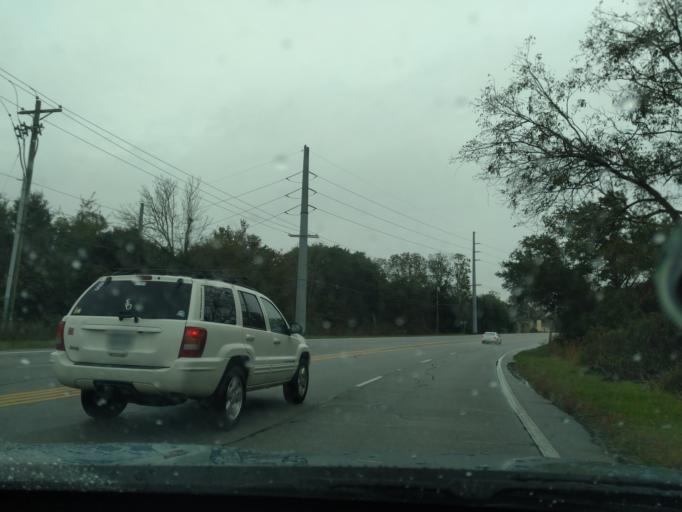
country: US
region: South Carolina
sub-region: Charleston County
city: Folly Beach
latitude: 32.6971
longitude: -79.9675
